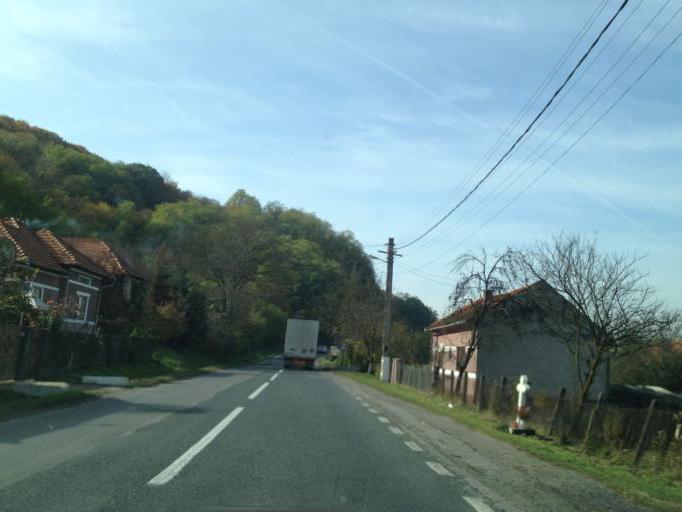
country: RO
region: Hunedoara
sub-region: Comuna Ilia
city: Ilia
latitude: 45.9181
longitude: 22.6413
